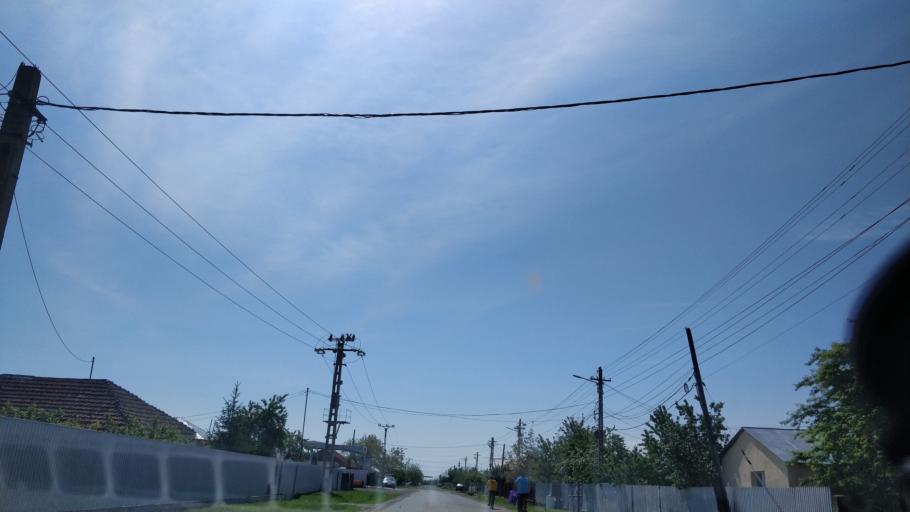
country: RO
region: Vrancea
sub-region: Comuna Suraia
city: Suraia
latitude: 45.6695
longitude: 27.3880
